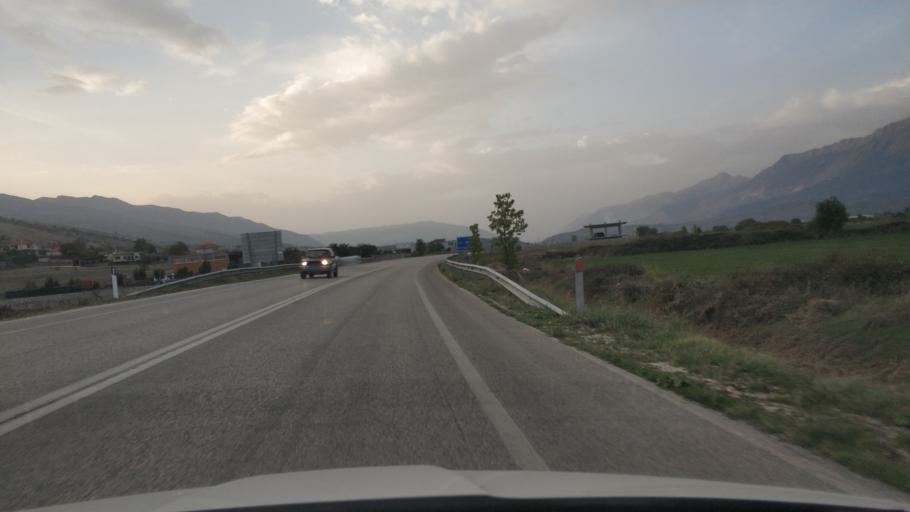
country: AL
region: Gjirokaster
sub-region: Rrethi i Gjirokastres
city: Dervician
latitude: 40.0167
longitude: 20.1962
